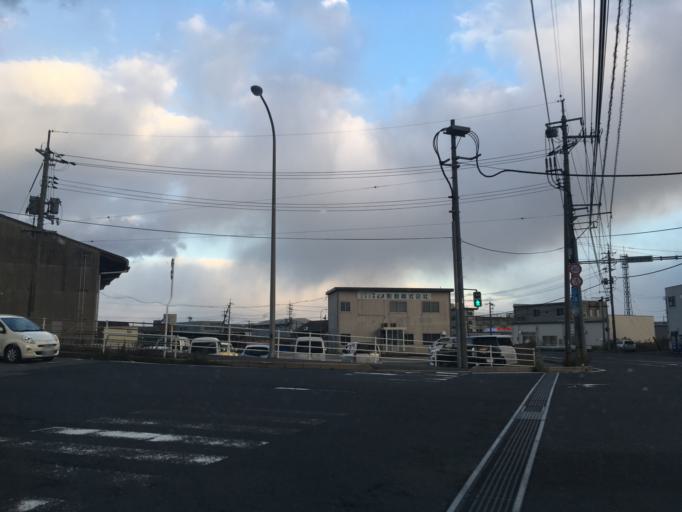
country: JP
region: Shimane
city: Matsue-shi
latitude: 35.4490
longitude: 133.1262
